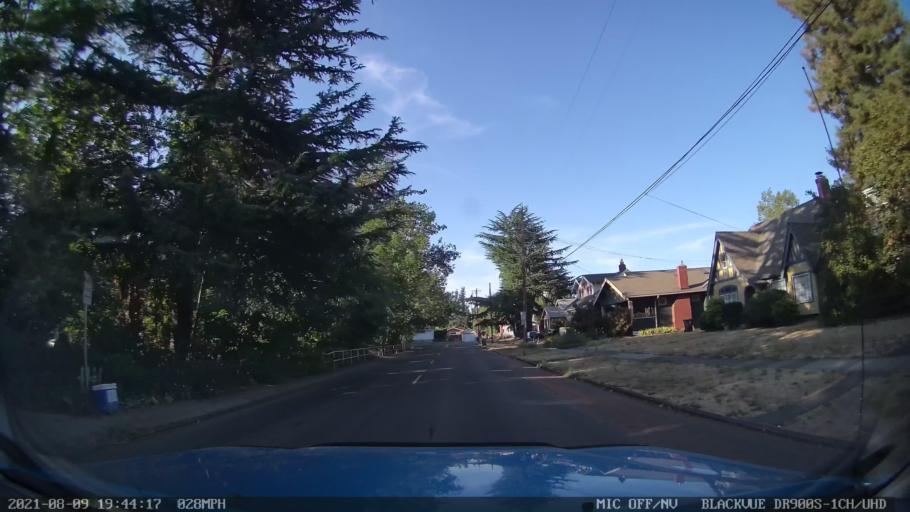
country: US
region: Oregon
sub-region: Marion County
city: Salem
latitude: 44.9469
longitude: -123.0315
